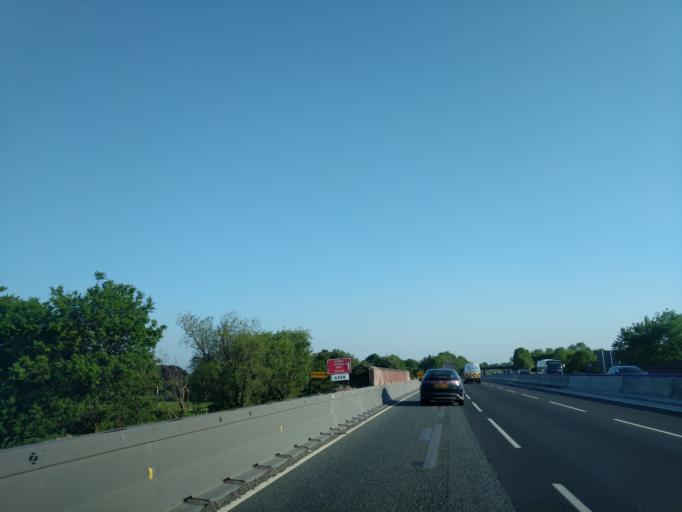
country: GB
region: England
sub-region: Cheshire East
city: Sandbach
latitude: 53.1207
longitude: -2.3350
